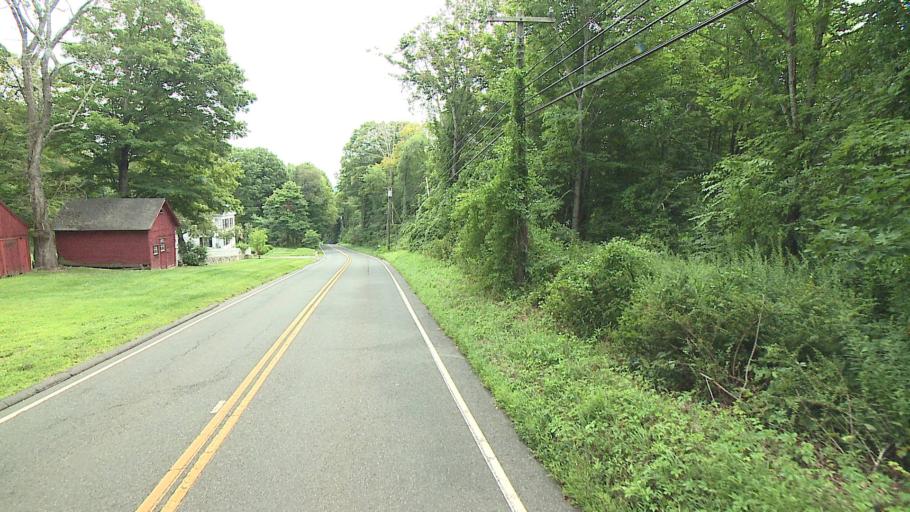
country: US
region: Connecticut
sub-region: Litchfield County
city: Woodbury
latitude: 41.5603
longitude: -73.2869
